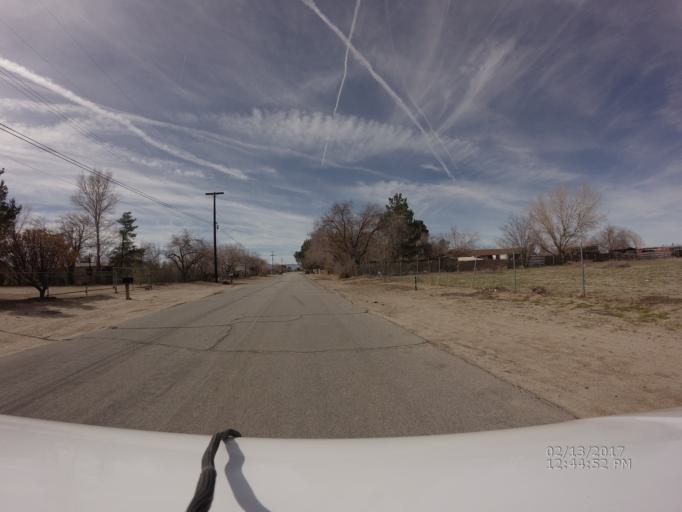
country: US
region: California
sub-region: Los Angeles County
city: Littlerock
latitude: 34.5689
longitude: -117.9267
